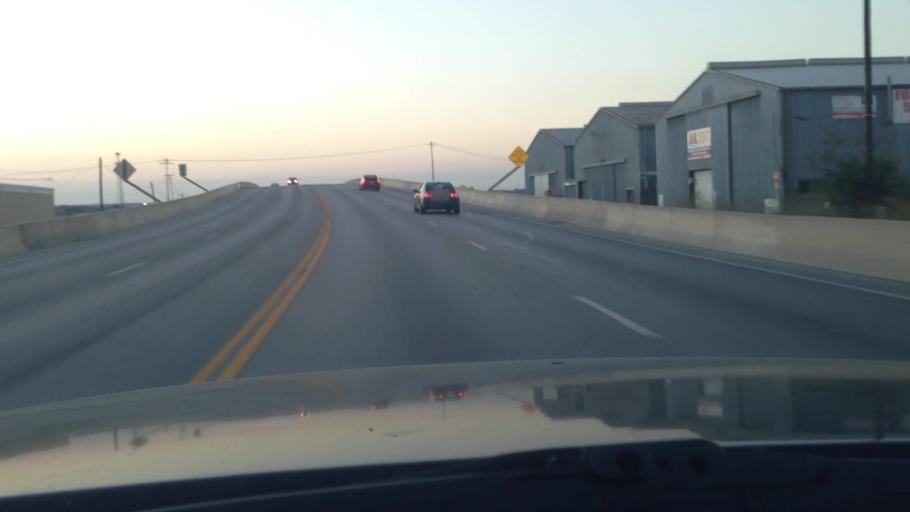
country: US
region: Texas
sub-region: Hays County
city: San Marcos
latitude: 29.8581
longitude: -97.9543
